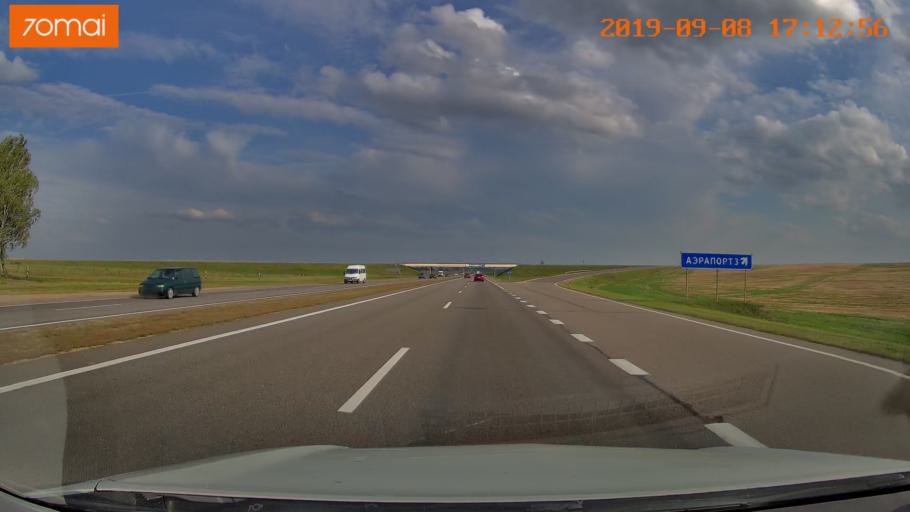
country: BY
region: Grodnenskaya
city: Skidal'
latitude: 53.6293
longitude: 24.0410
